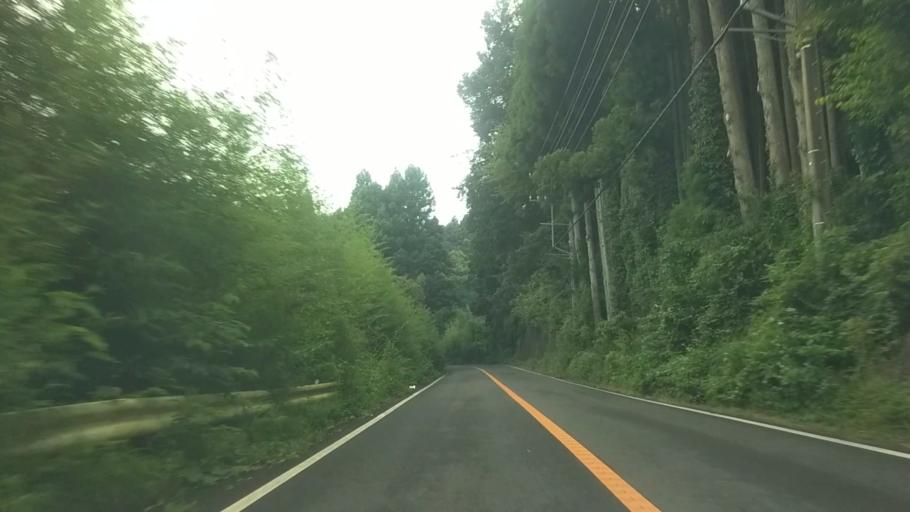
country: JP
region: Chiba
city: Kawaguchi
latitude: 35.2341
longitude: 140.0728
